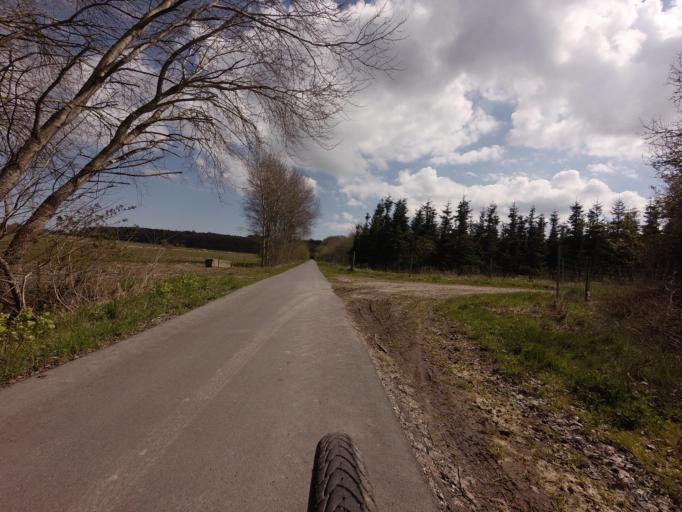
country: DK
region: North Denmark
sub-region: Mariagerfjord Kommune
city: Hadsund
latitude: 56.8459
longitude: 10.1031
